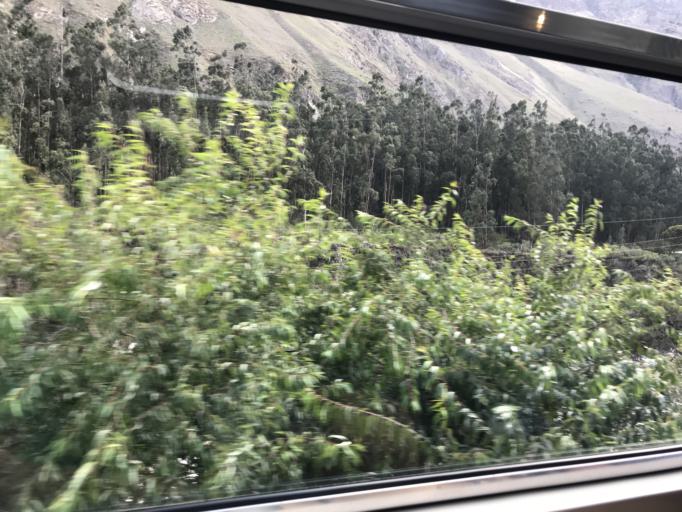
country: PE
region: Cusco
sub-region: Provincia de Urubamba
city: Ollantaytambo
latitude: -13.2256
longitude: -72.4327
